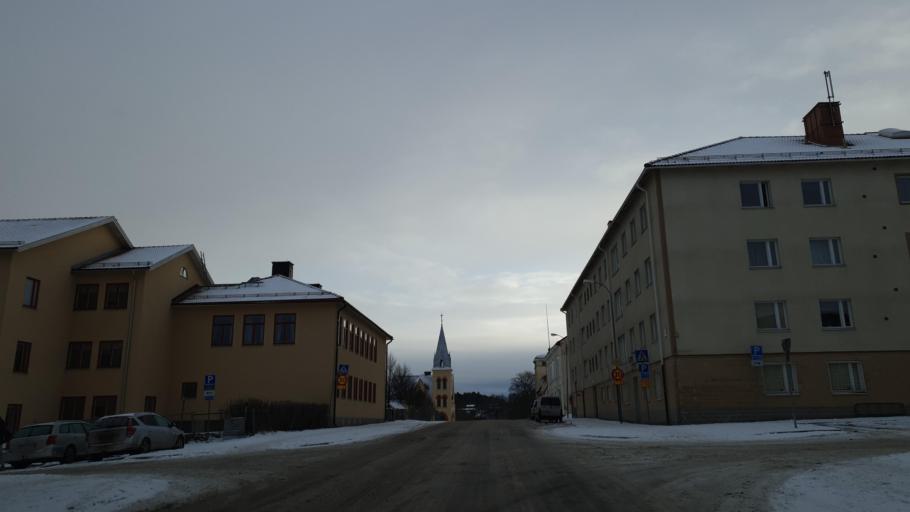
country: SE
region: Gaevleborg
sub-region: Soderhamns Kommun
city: Soderhamn
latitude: 61.3061
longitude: 17.0538
